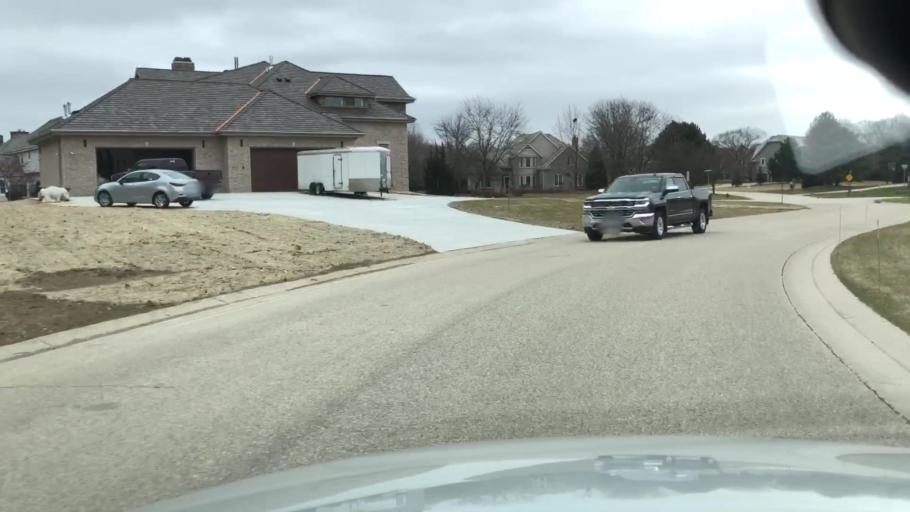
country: US
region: Wisconsin
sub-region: Waukesha County
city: Brookfield
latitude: 43.0723
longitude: -88.1718
